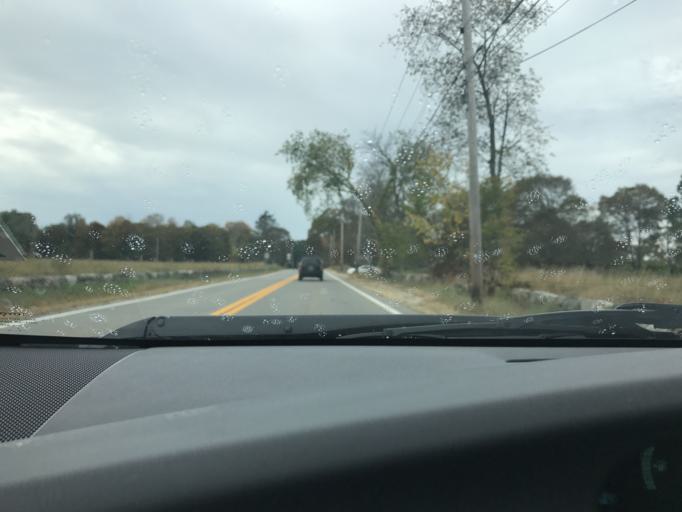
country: US
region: Massachusetts
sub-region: Middlesex County
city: Lincoln
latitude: 42.4530
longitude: -71.3067
